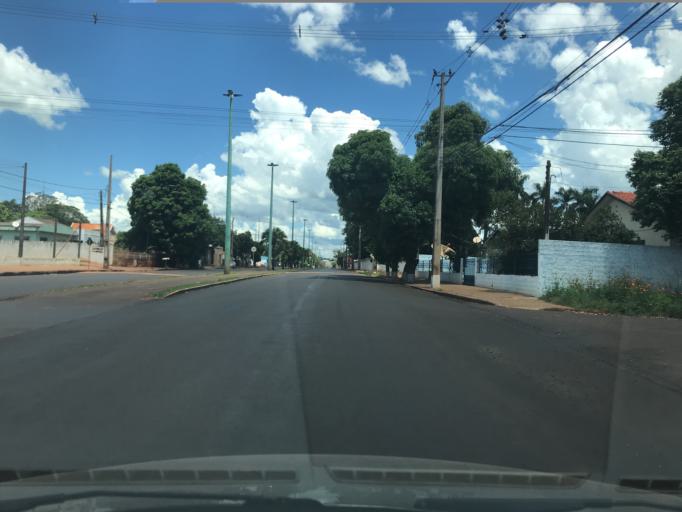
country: BR
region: Parana
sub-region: Palotina
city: Palotina
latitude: -24.2720
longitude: -53.8417
